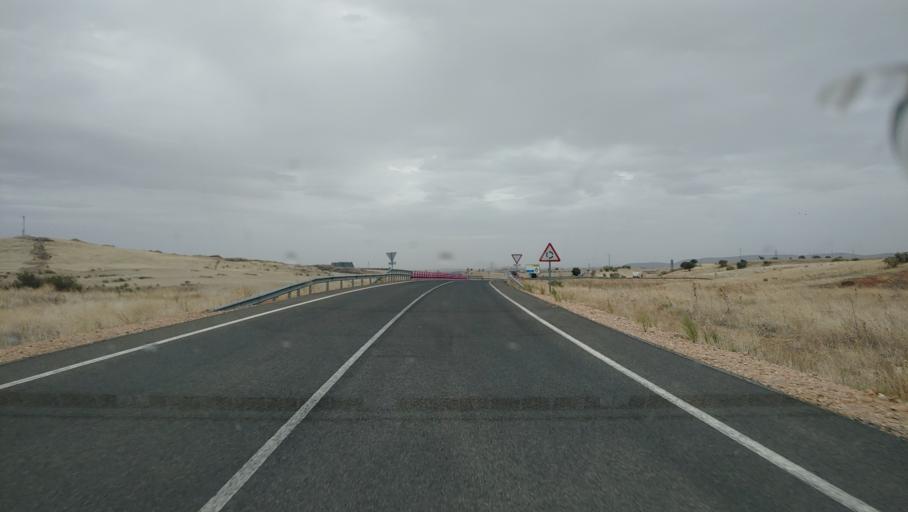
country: ES
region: Castille-La Mancha
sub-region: Provincia de Ciudad Real
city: Canada de Calatrava
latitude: 38.8752
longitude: -4.0104
